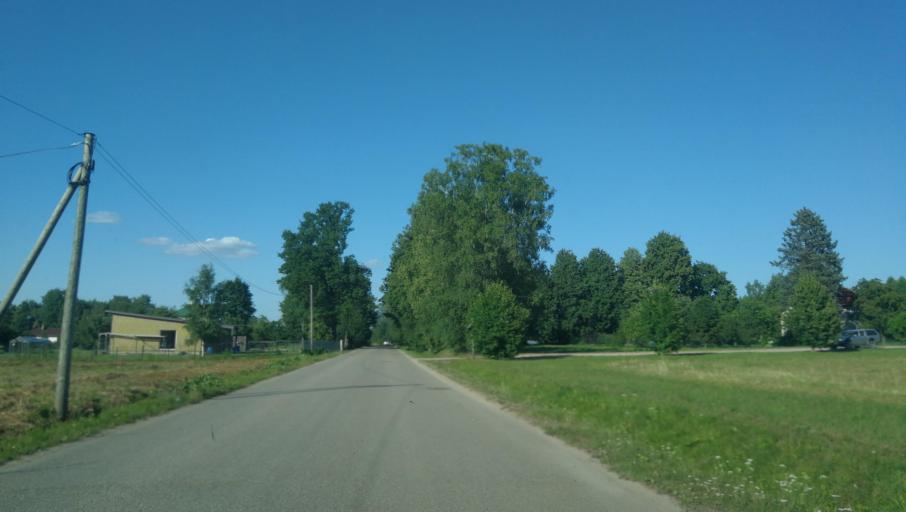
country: LV
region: Cesu Rajons
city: Cesis
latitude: 57.2971
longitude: 25.2370
